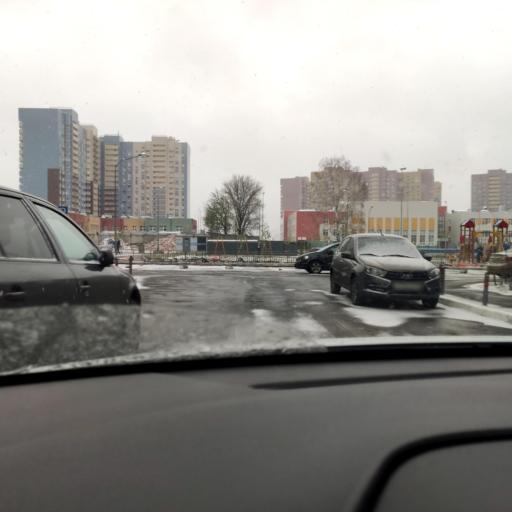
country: RU
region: Tatarstan
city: Osinovo
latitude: 55.8675
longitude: 48.8789
